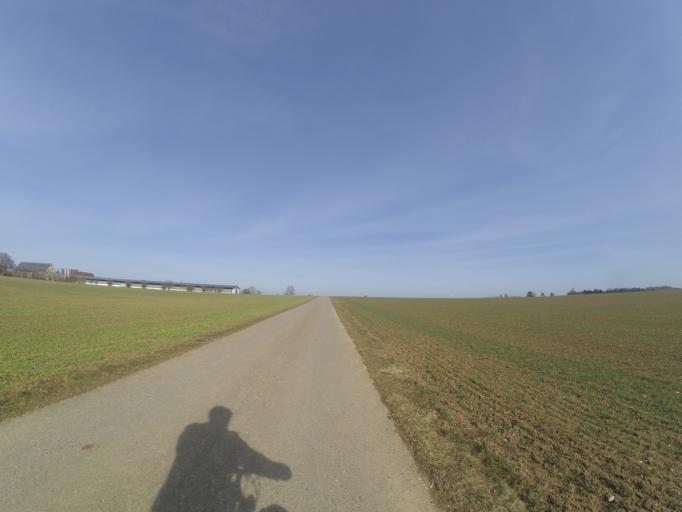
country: DE
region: Baden-Wuerttemberg
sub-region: Tuebingen Region
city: Beimerstetten
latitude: 48.4680
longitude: 9.9963
